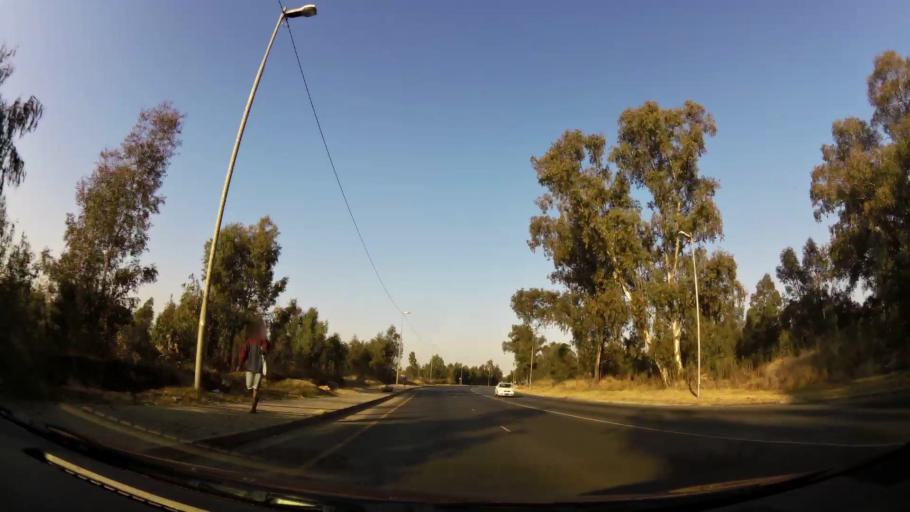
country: ZA
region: Gauteng
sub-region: City of Johannesburg Metropolitan Municipality
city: Johannesburg
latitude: -26.2129
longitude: 27.9884
